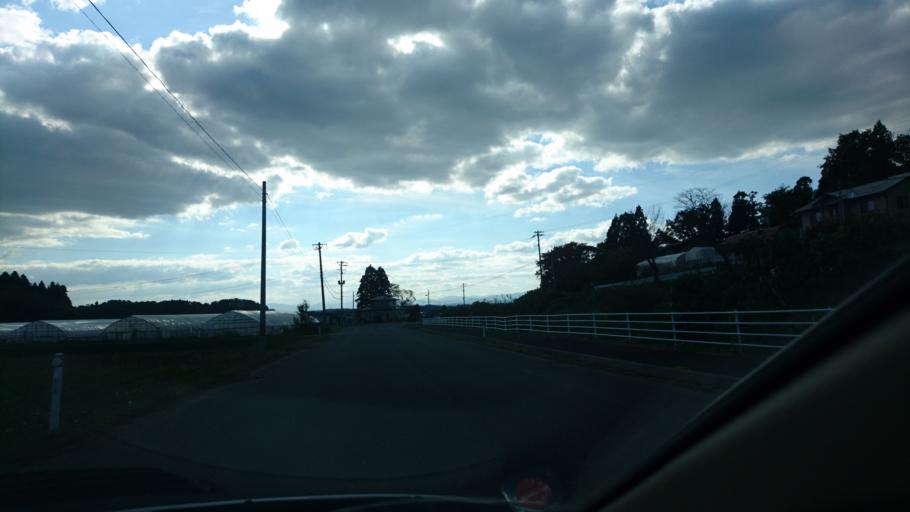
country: JP
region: Iwate
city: Kitakami
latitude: 39.2458
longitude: 141.1281
